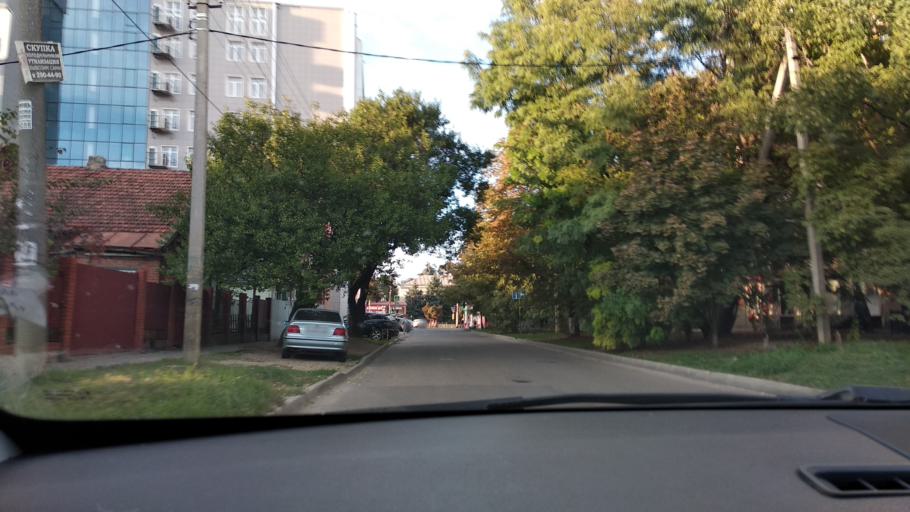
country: RU
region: Krasnodarskiy
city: Krasnodar
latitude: 45.0191
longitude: 39.0044
